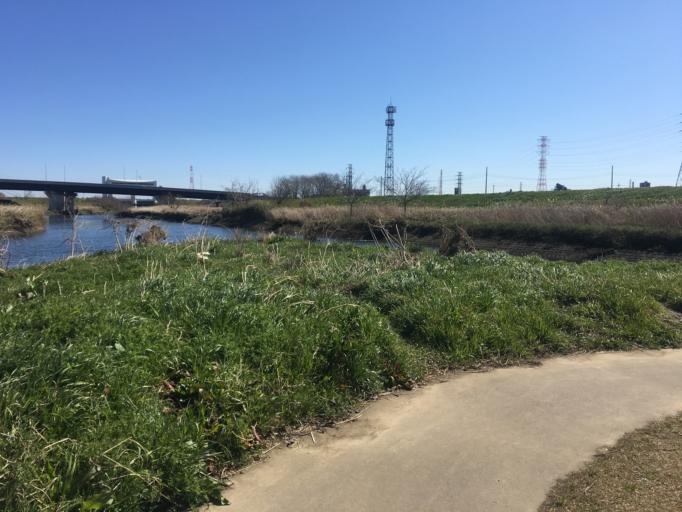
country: JP
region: Saitama
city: Asaka
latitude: 35.8131
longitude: 139.6115
